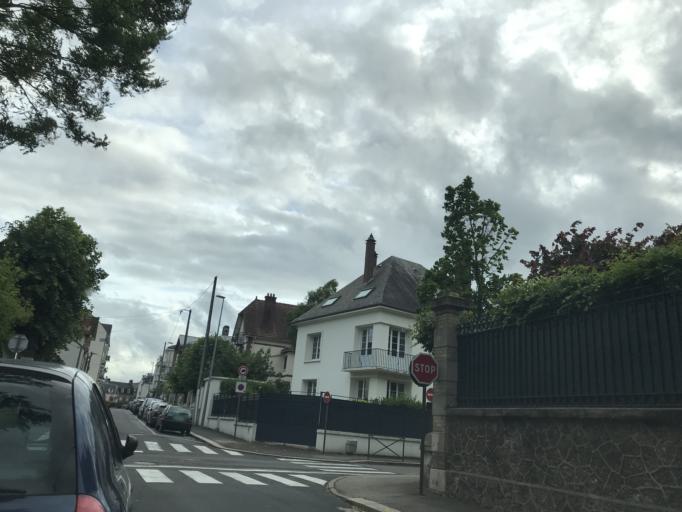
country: FR
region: Ile-de-France
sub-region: Departement des Yvelines
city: Mantes-la-Jolie
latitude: 48.9921
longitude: 1.7122
